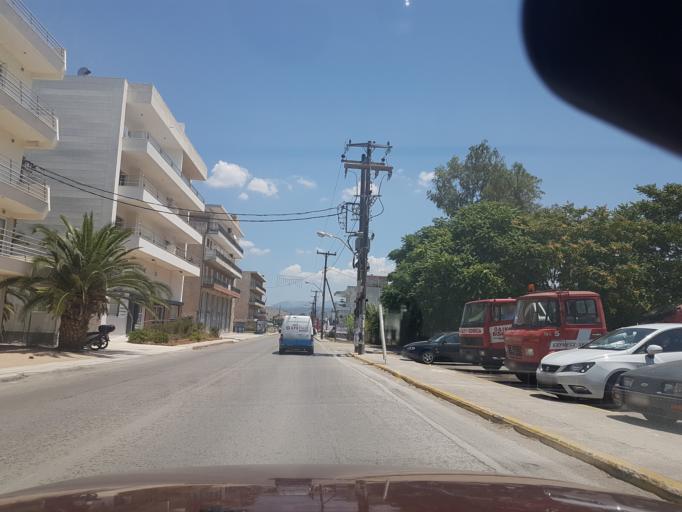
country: GR
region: Central Greece
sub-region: Nomos Evvoias
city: Chalkida
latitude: 38.4696
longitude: 23.6123
